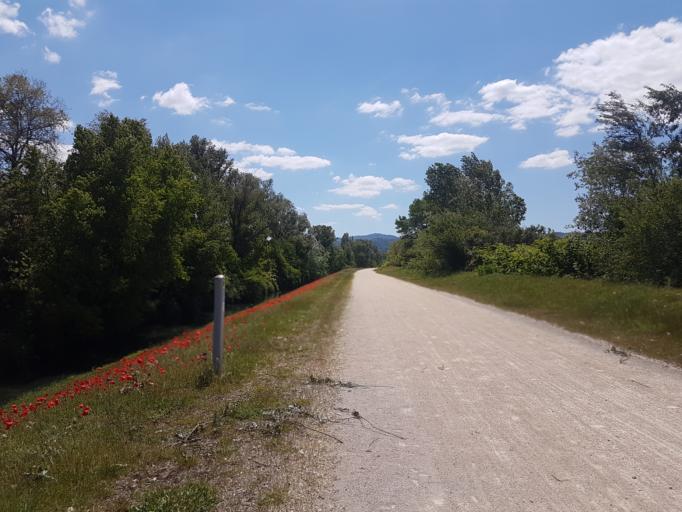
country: FR
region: Rhone-Alpes
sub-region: Departement de l'Ardeche
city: Tournon-sur-Rhone
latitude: 45.0490
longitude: 4.8587
